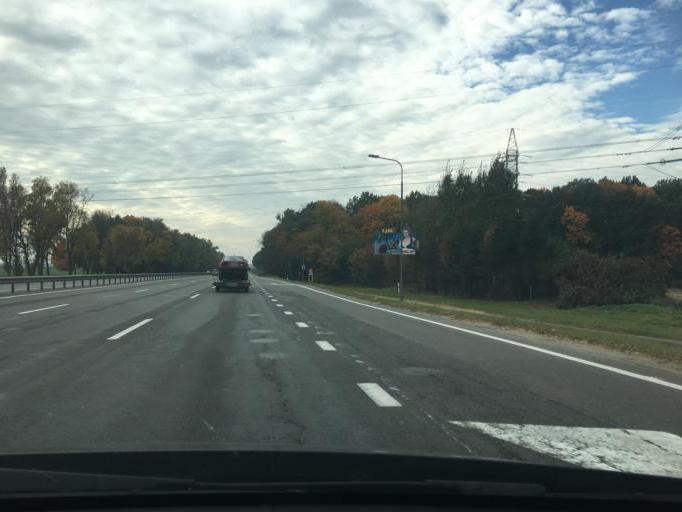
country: BY
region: Minsk
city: Shchomyslitsa
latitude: 53.8163
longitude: 27.4276
